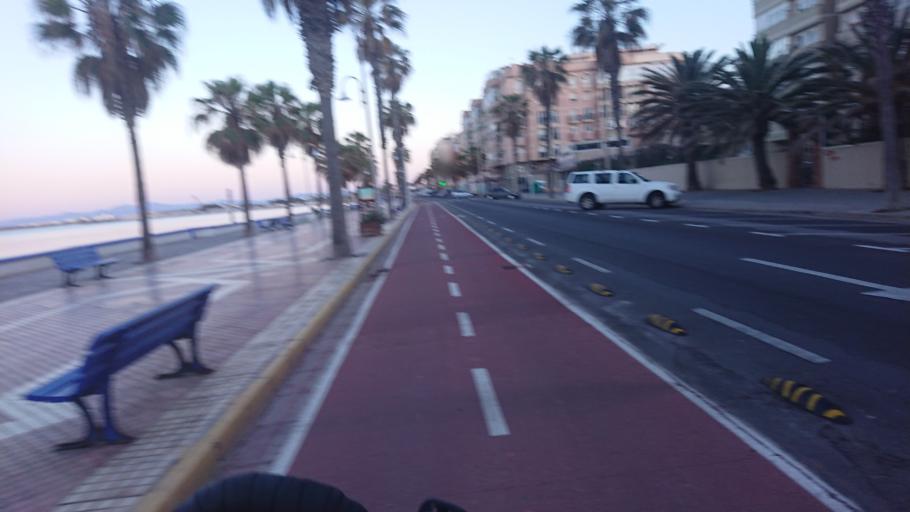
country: ES
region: Melilla
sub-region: Melilla
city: Melilla
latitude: 35.2820
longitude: -2.9378
